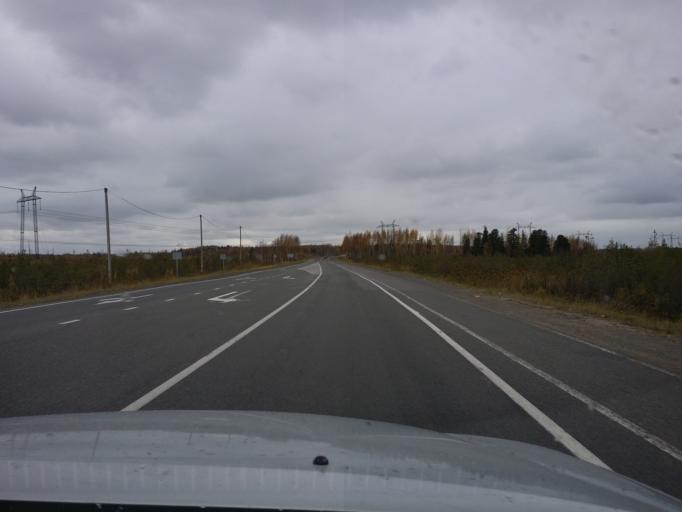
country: RU
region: Khanty-Mansiyskiy Avtonomnyy Okrug
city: Megion
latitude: 61.1091
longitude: 76.0149
